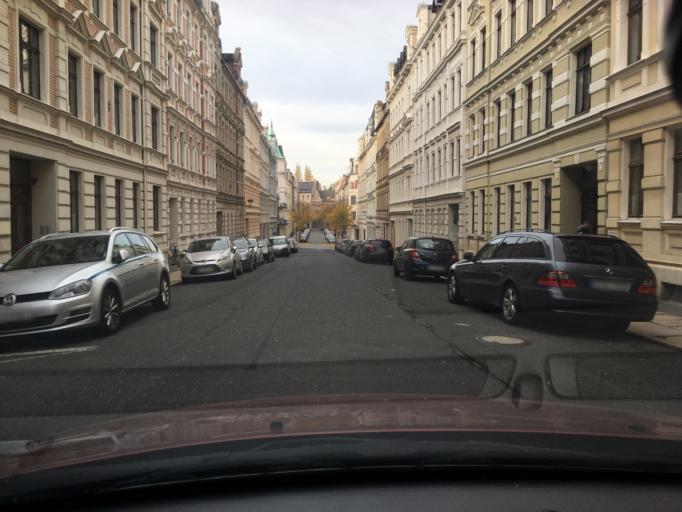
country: DE
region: Saxony
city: Goerlitz
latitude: 51.1510
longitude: 14.9752
